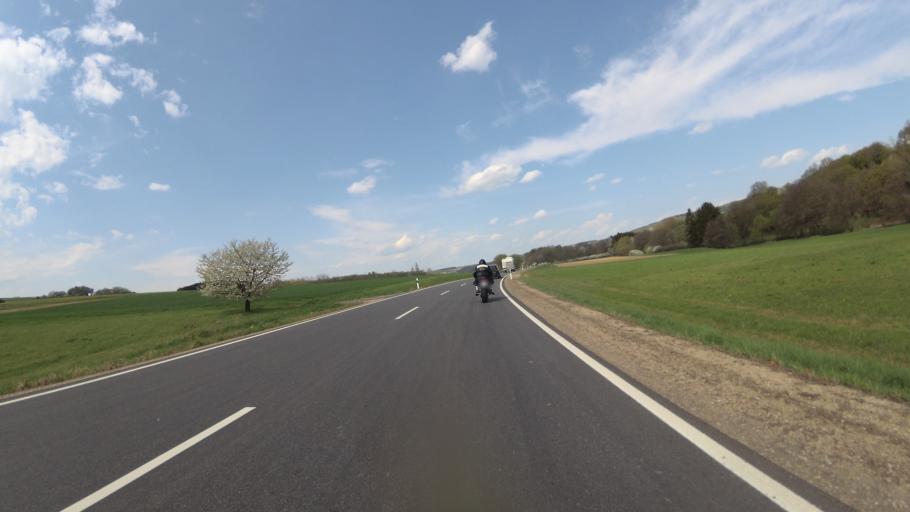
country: DE
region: Rheinland-Pfalz
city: Mullenbach
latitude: 50.3050
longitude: 6.9092
